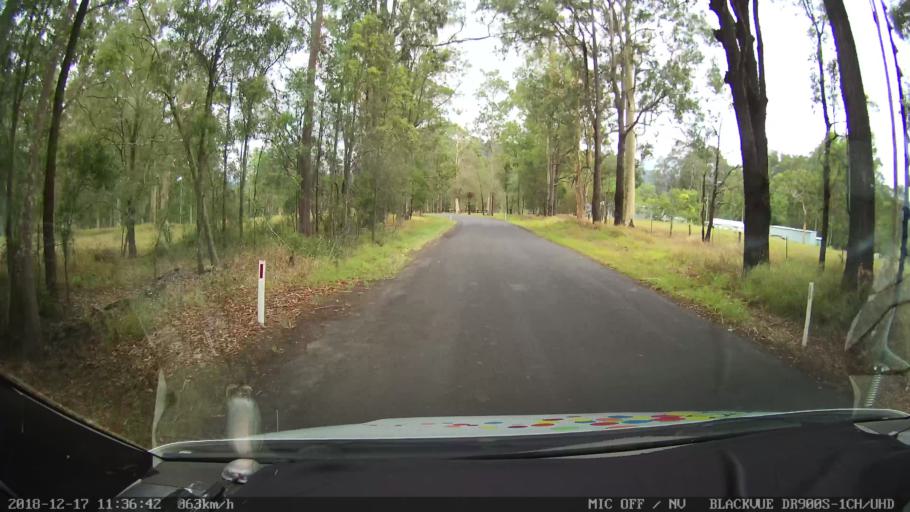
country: AU
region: New South Wales
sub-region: Kyogle
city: Kyogle
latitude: -28.7116
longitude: 152.6060
